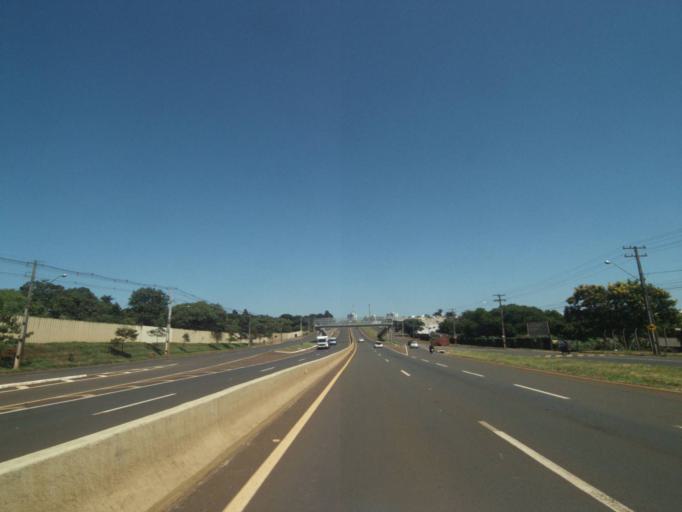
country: BR
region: Parana
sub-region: Londrina
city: Londrina
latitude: -23.3550
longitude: -51.1602
